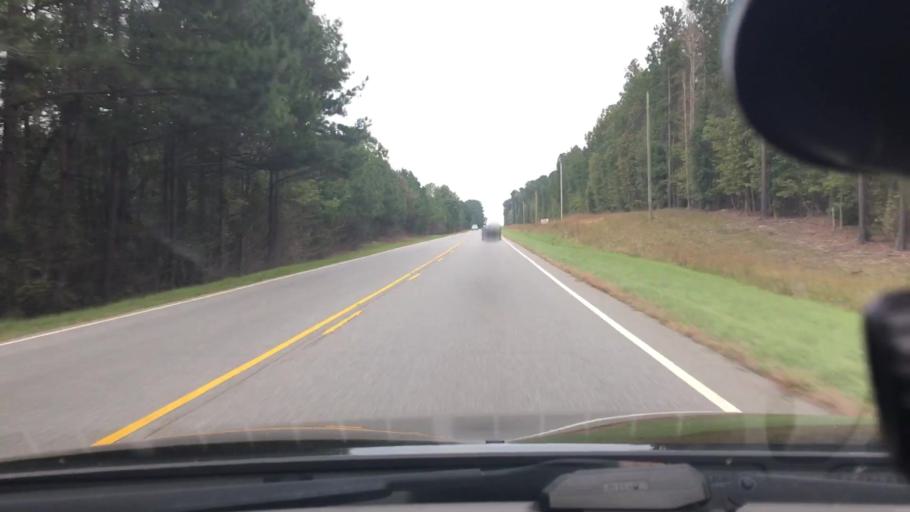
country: US
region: North Carolina
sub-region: Montgomery County
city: Biscoe
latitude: 35.3674
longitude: -79.6787
